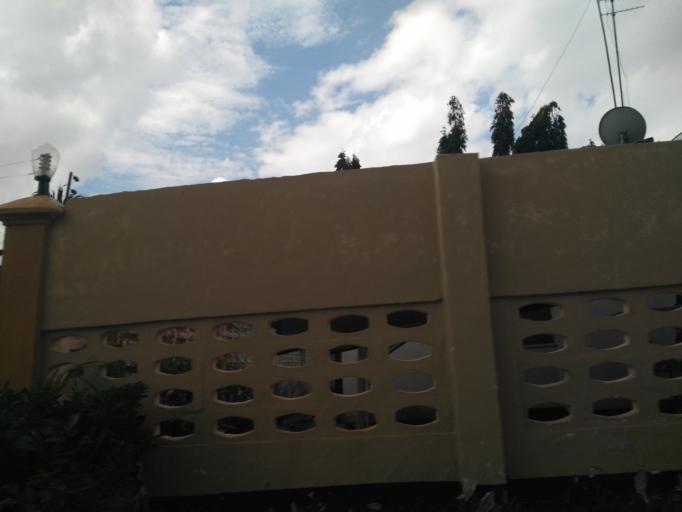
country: TZ
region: Dar es Salaam
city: Magomeni
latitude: -6.7614
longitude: 39.2435
